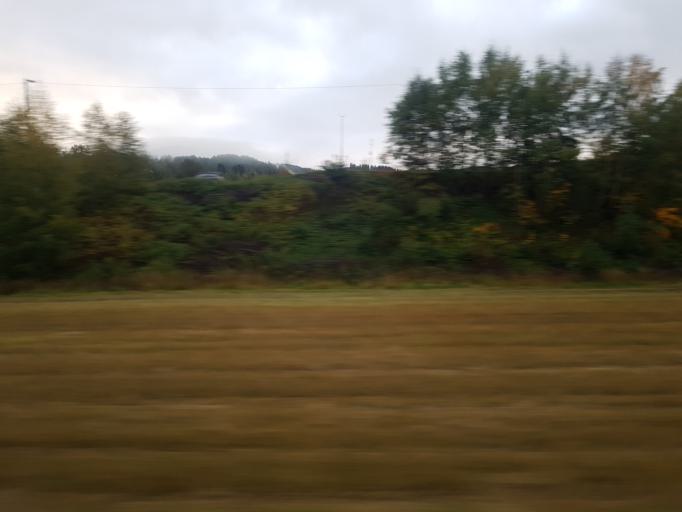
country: NO
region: Sor-Trondelag
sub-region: Melhus
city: Lundamo
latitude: 63.1279
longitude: 10.2485
